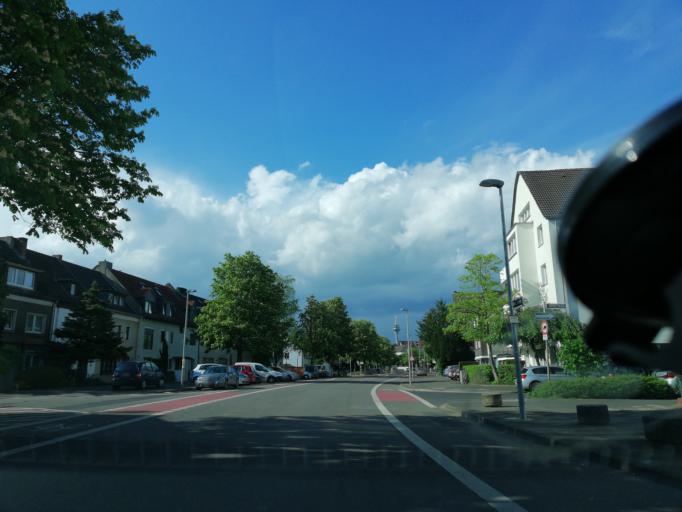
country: DE
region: North Rhine-Westphalia
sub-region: Regierungsbezirk Dusseldorf
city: Dusseldorf
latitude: 51.1974
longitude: 6.7679
